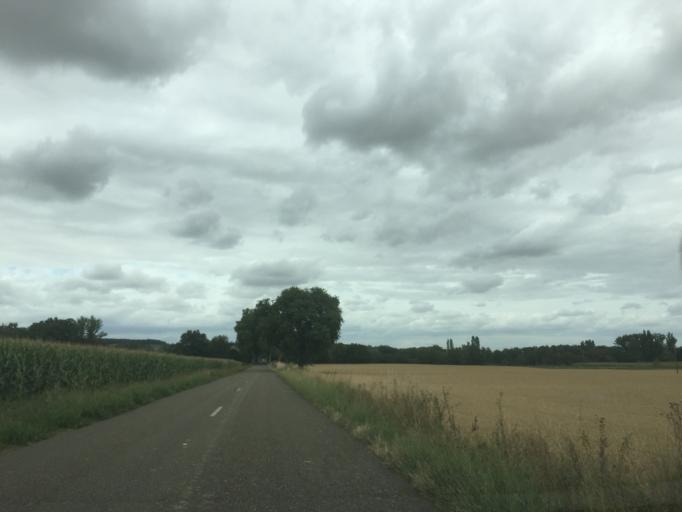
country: FR
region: Midi-Pyrenees
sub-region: Departement du Gers
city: Vic-Fezensac
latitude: 43.7440
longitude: 0.3773
